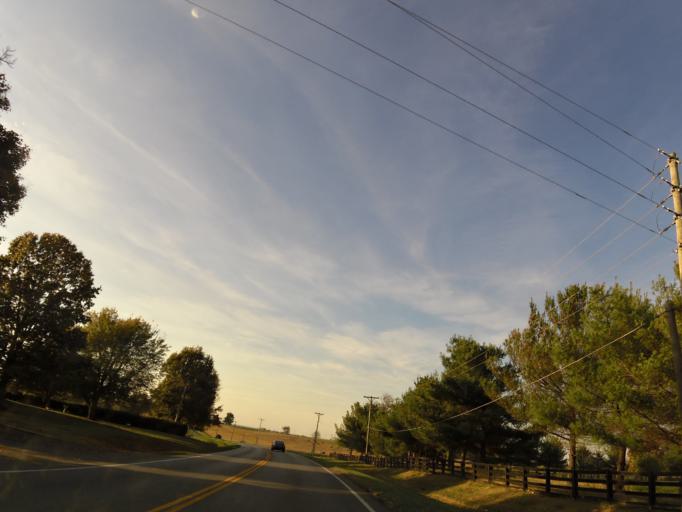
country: US
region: Kentucky
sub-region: Garrard County
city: Lancaster
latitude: 37.6808
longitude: -84.6492
